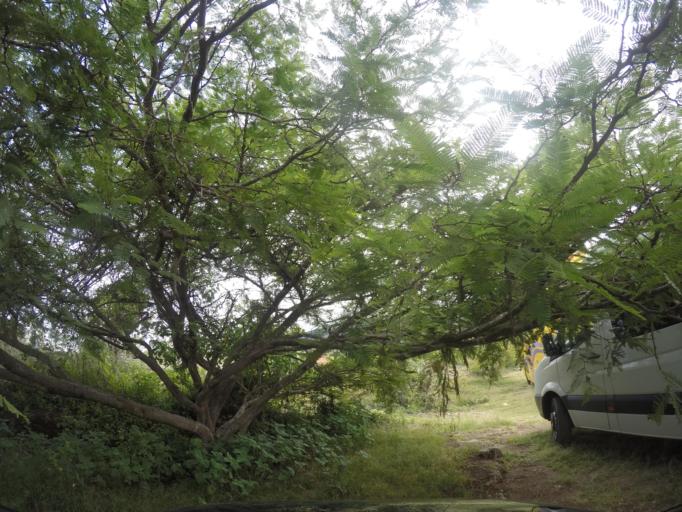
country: MX
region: Oaxaca
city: San Lorenzo Albarradas
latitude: 16.8676
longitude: -96.2765
